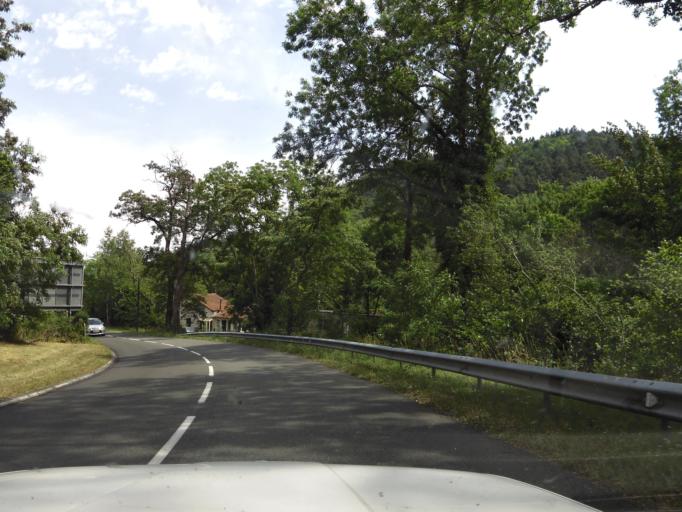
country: FR
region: Auvergne
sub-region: Departement du Puy-de-Dome
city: Royat
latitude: 45.7656
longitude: 3.0333
